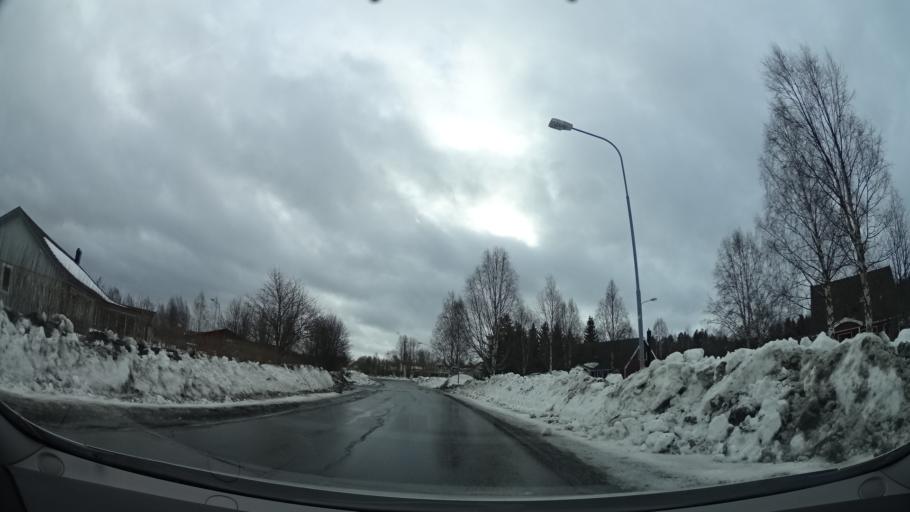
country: SE
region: Vaesterbotten
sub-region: Skelleftea Kommun
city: Soedra Bergsbyn
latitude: 64.7545
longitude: 21.0380
